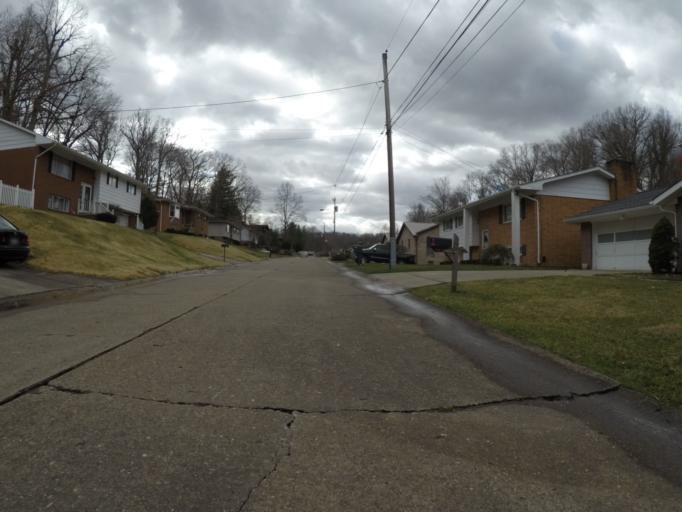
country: US
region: West Virginia
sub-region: Cabell County
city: Pea Ridge
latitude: 38.4070
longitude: -82.3816
